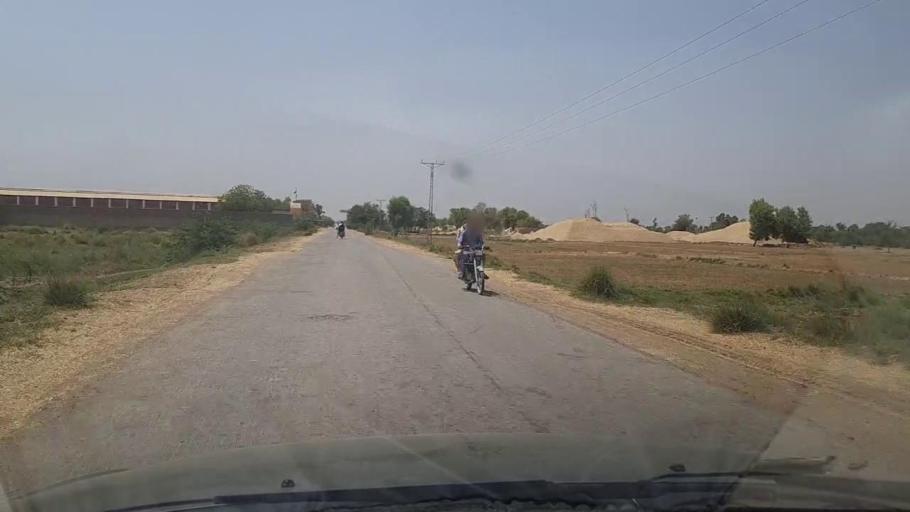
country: PK
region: Sindh
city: Karaundi
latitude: 26.8795
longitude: 68.3130
